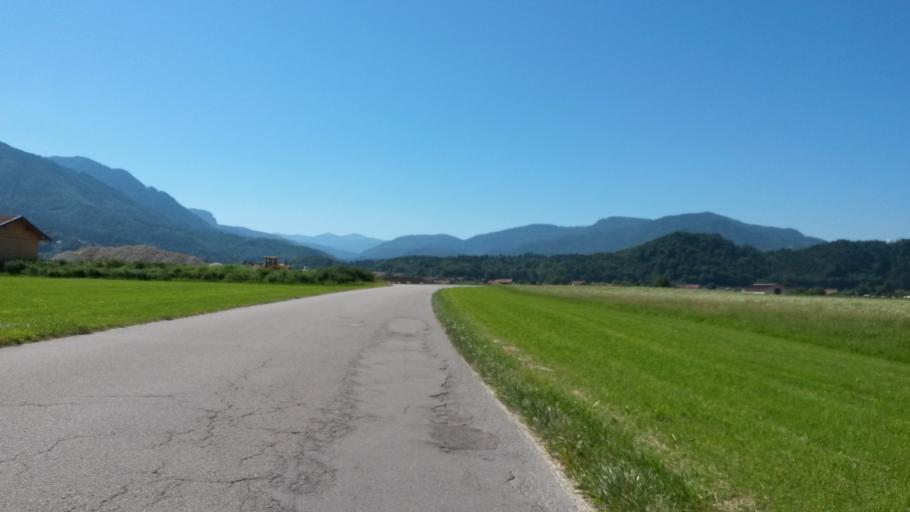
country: DE
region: Bavaria
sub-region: Upper Bavaria
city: Grassau
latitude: 47.7720
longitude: 12.4553
